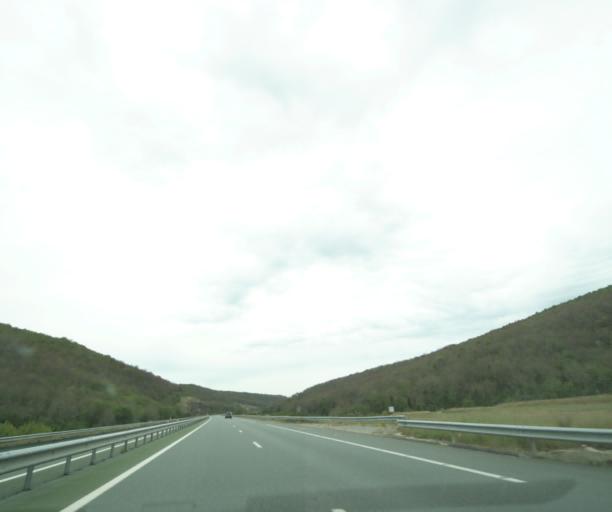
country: FR
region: Midi-Pyrenees
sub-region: Departement du Lot
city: Souillac
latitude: 44.8182
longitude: 1.4996
